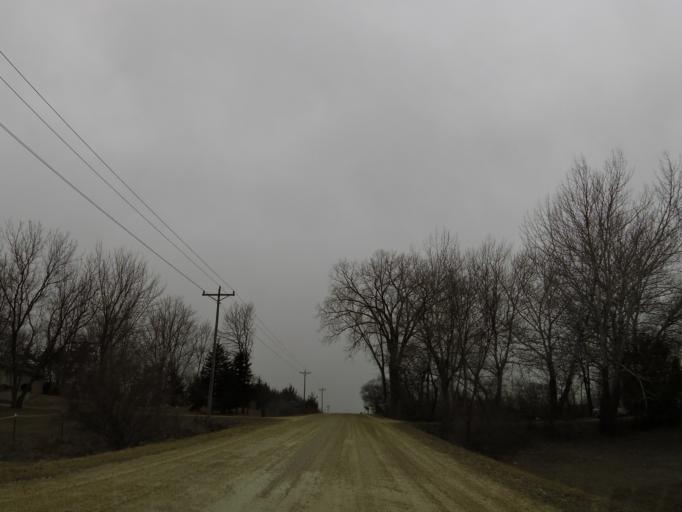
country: US
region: Minnesota
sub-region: Scott County
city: Prior Lake
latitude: 44.6886
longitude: -93.4504
